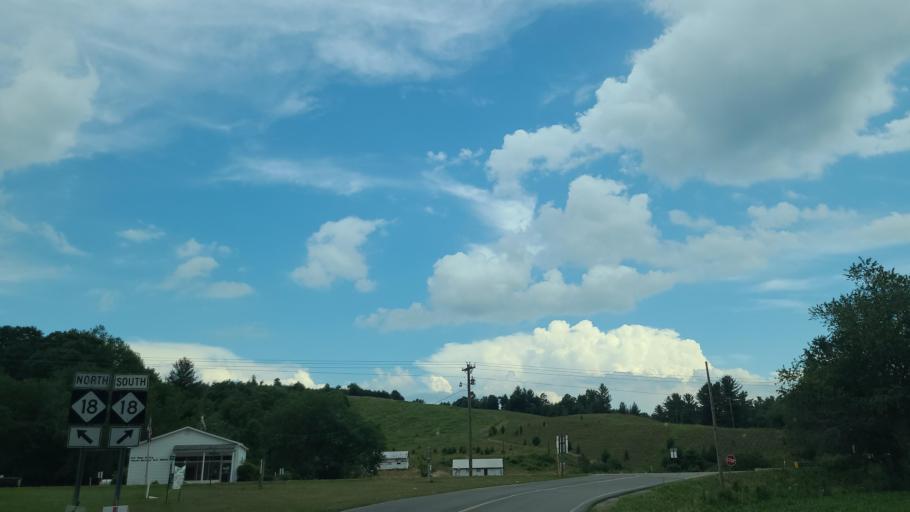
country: US
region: North Carolina
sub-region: Alleghany County
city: Sparta
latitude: 36.4129
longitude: -81.2641
